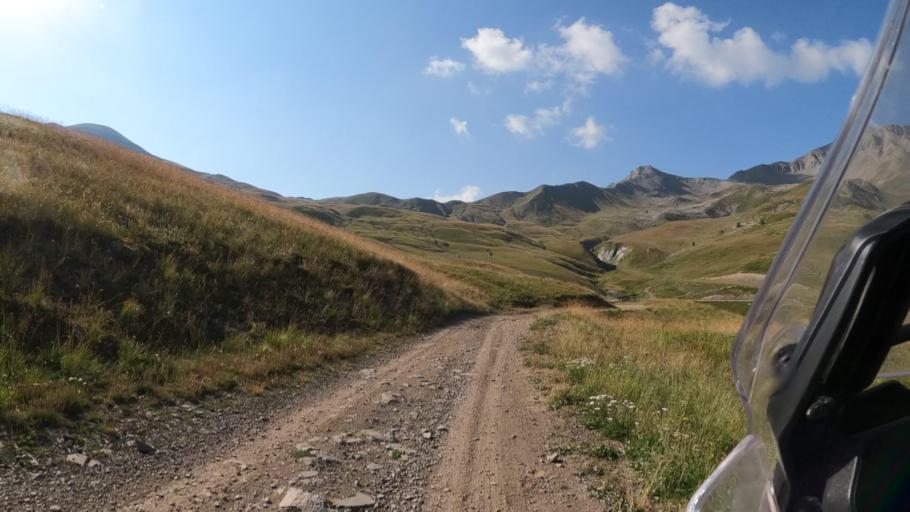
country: FR
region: Provence-Alpes-Cote d'Azur
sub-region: Departement des Hautes-Alpes
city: Guillestre
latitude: 44.5897
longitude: 6.6410
